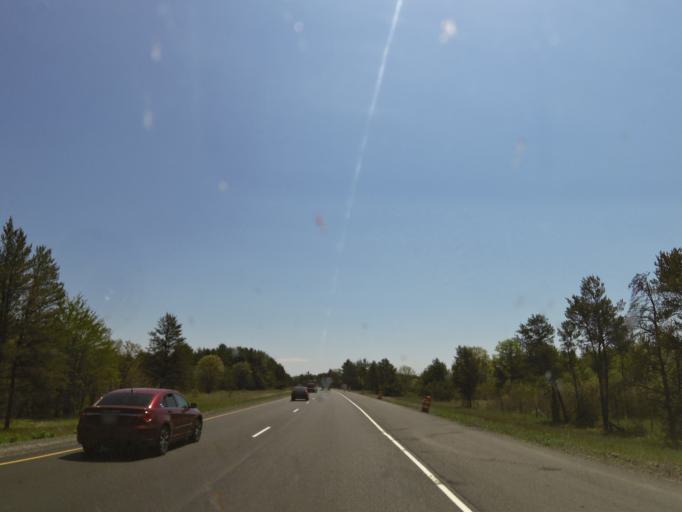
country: US
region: Wisconsin
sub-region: Jackson County
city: Black River Falls
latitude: 44.2474
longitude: -90.7465
